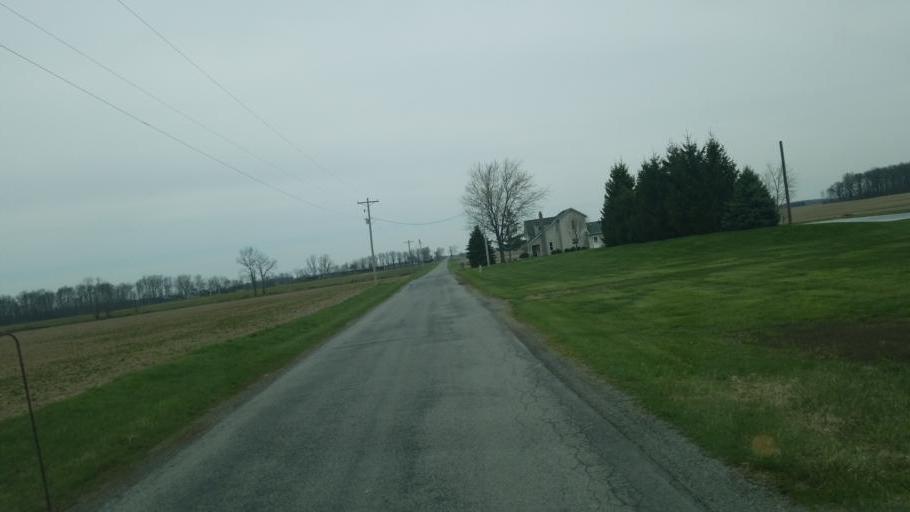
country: US
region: Ohio
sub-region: Hardin County
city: Forest
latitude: 40.9069
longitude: -83.5147
